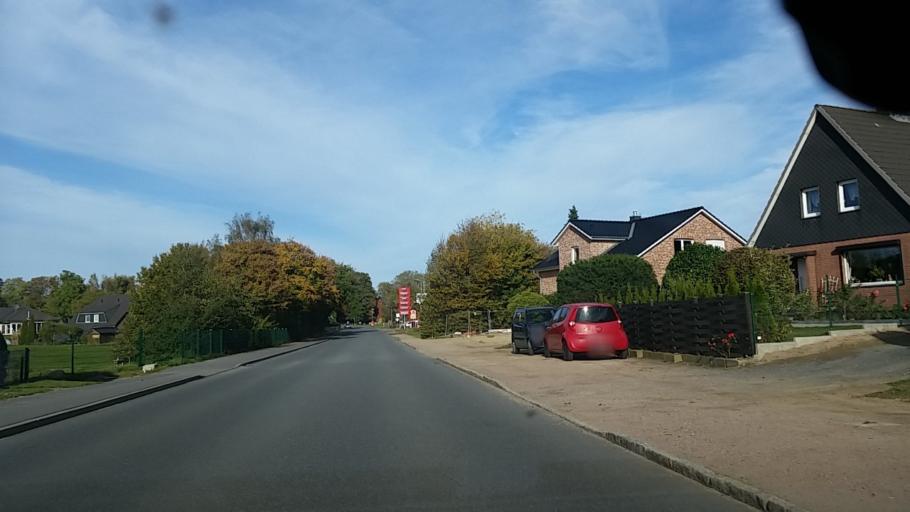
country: DE
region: Schleswig-Holstein
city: Delingsdorf
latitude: 53.7041
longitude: 10.2506
